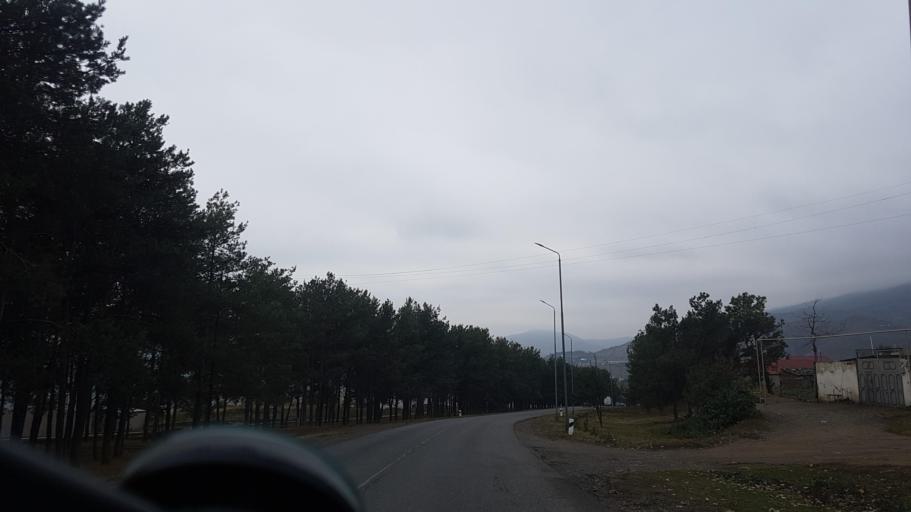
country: AZ
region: Gadabay Rayon
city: Ariqdam
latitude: 40.6046
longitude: 45.8123
